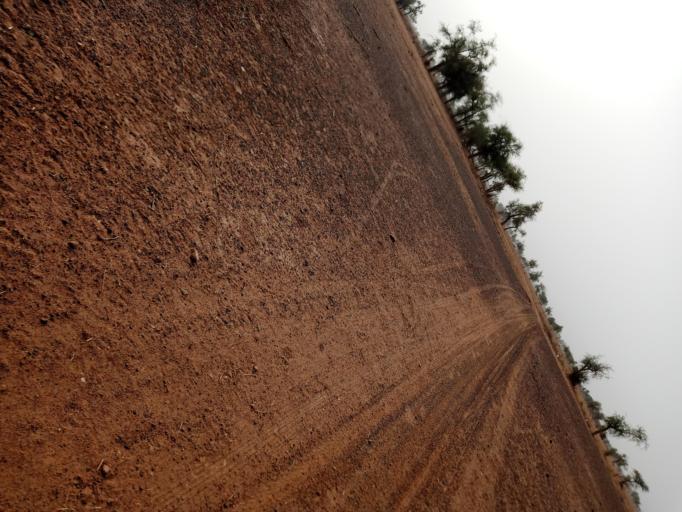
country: BF
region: Est
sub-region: Gnagna Province
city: Bogande
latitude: 13.2776
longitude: -0.1561
